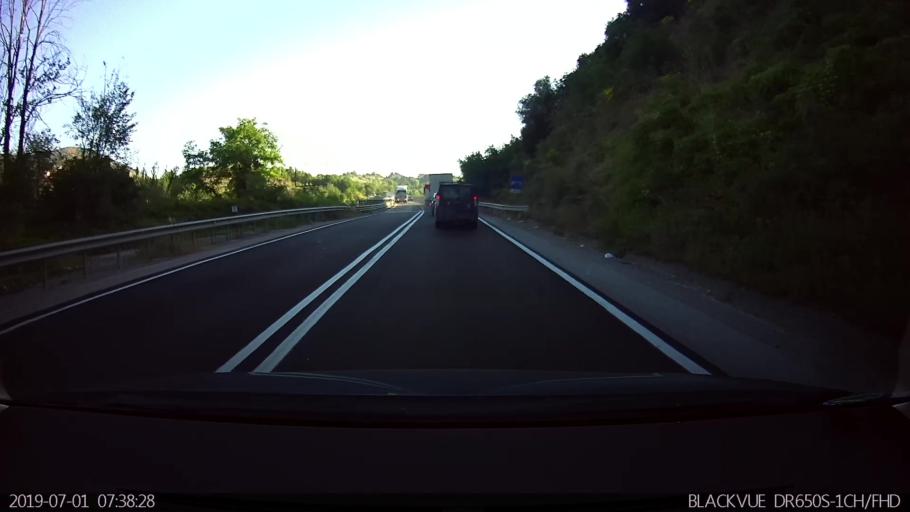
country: IT
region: Latium
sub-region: Provincia di Frosinone
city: Giuliano di Roma
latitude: 41.5438
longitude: 13.2688
